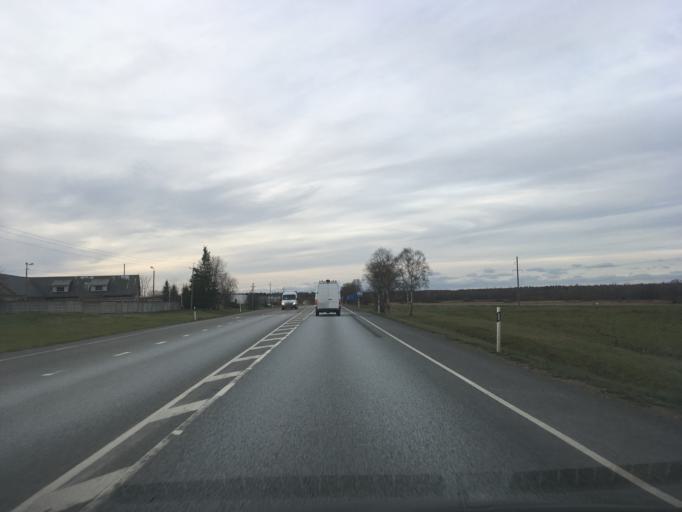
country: EE
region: Ida-Virumaa
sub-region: Kohtla-Jaerve linn
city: Kohtla-Jarve
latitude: 59.4093
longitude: 27.3142
